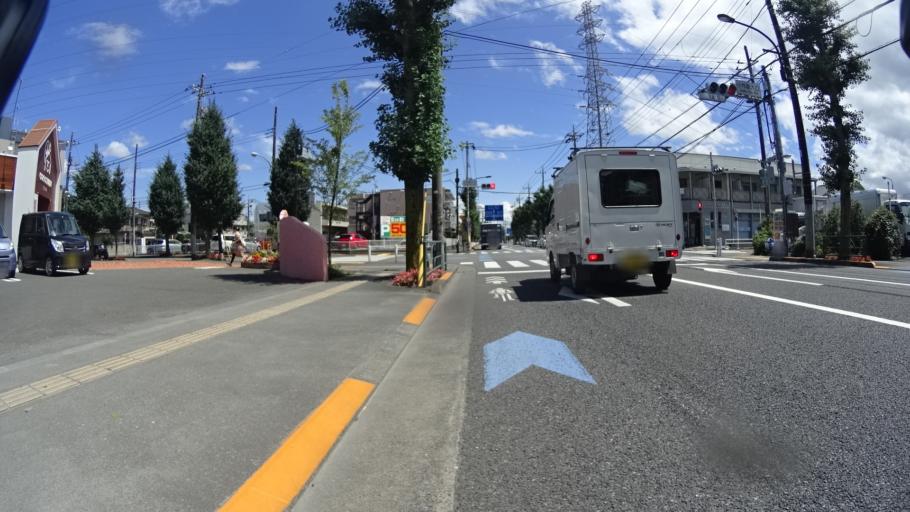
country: JP
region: Tokyo
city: Fussa
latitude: 35.7750
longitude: 139.2998
